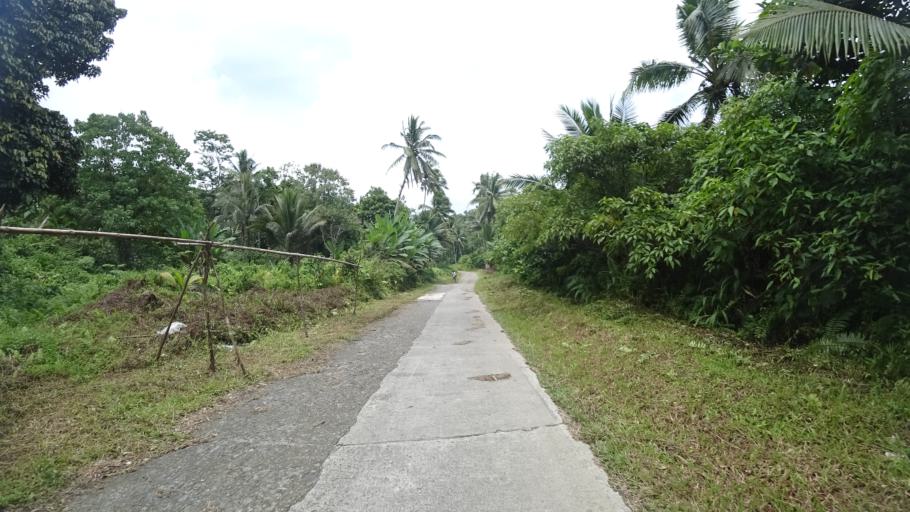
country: PH
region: Eastern Visayas
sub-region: Province of Leyte
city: Bugho
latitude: 10.8274
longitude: 124.8998
